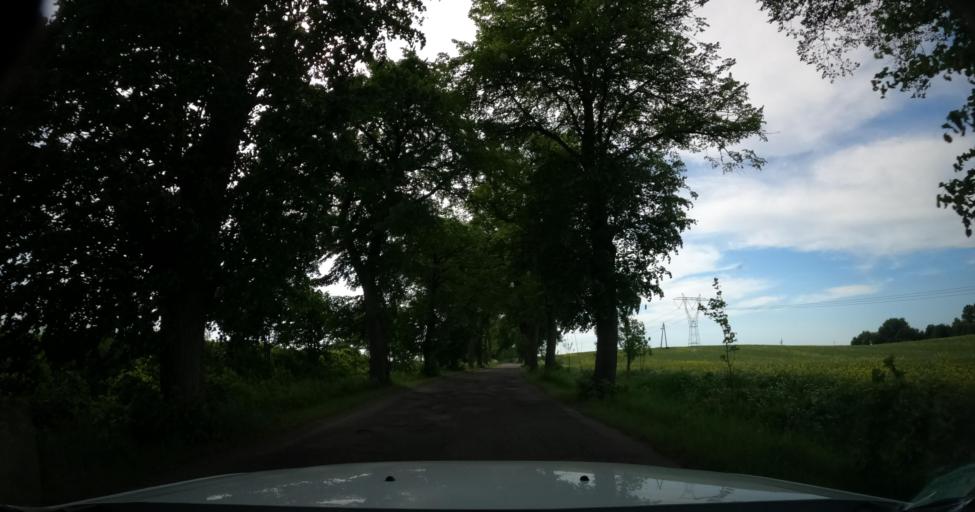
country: PL
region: Warmian-Masurian Voivodeship
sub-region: Powiat ostrodzki
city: Milakowo
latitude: 54.0180
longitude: 20.0432
